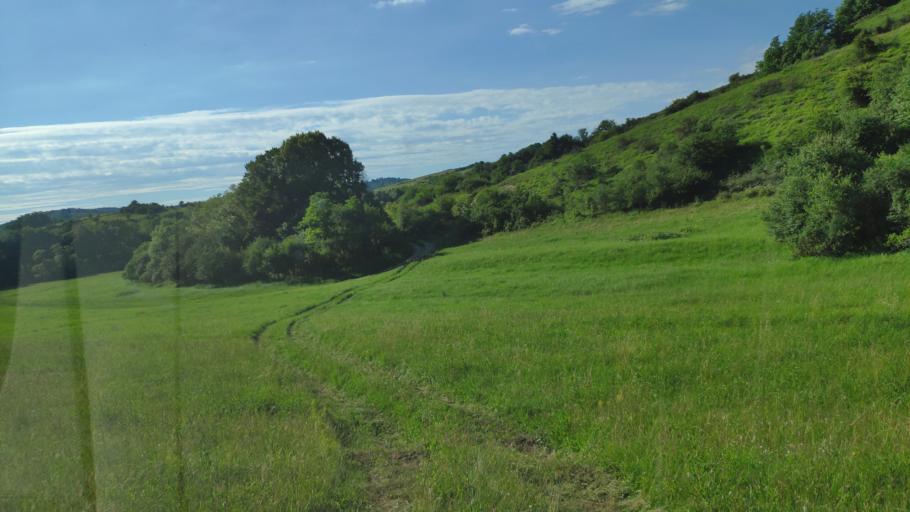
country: SK
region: Banskobystricky
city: Rimavska Sobota
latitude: 48.2472
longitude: 20.1089
